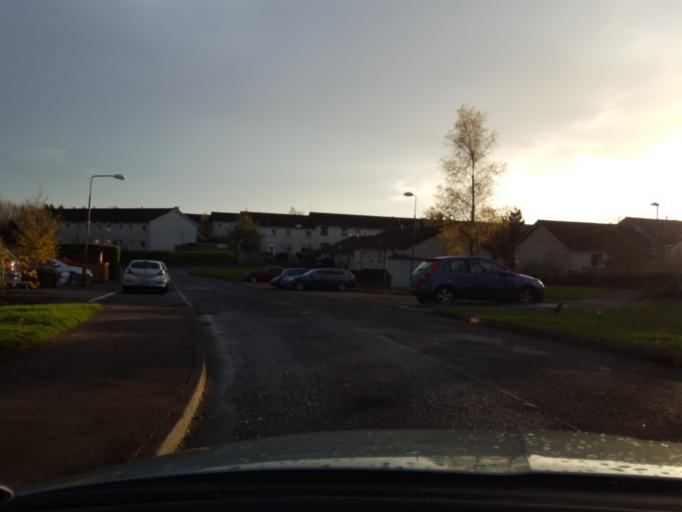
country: GB
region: Scotland
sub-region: West Lothian
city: Livingston
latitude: 55.9060
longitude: -3.5391
